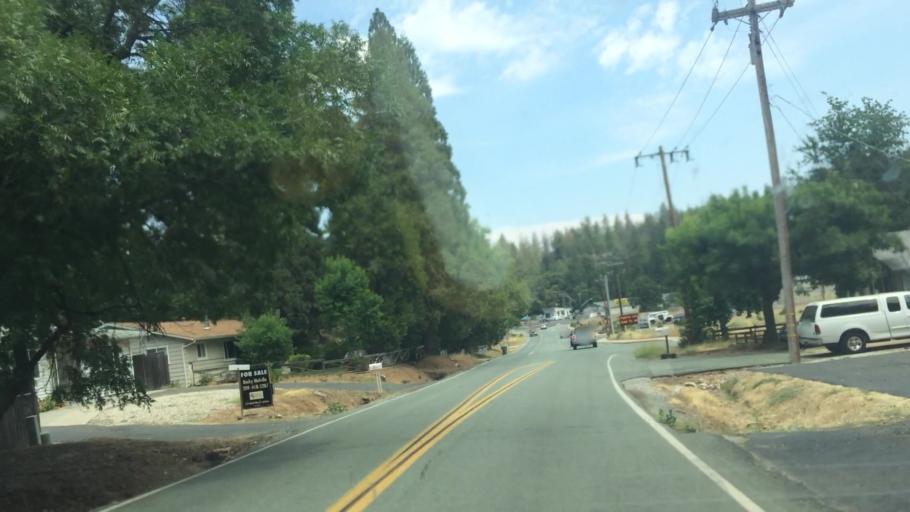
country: US
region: California
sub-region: Amador County
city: Pine Grove
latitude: 38.4138
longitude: -120.6707
